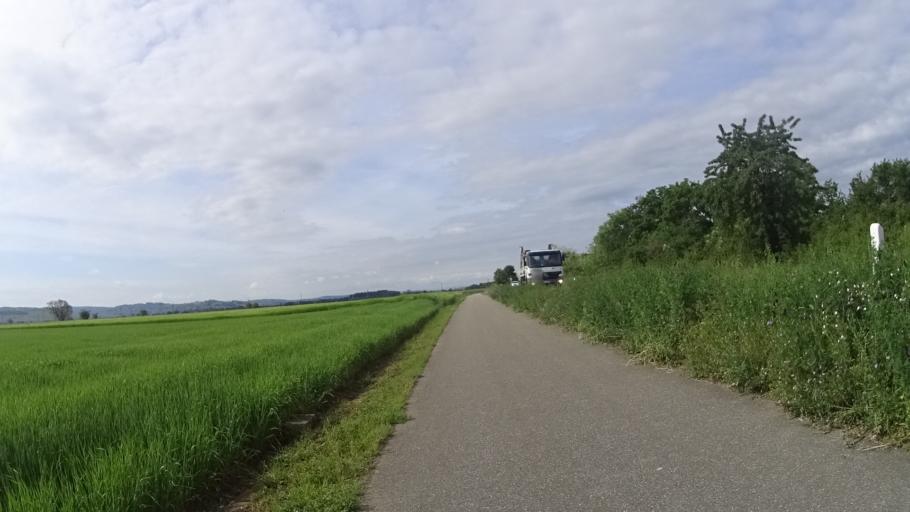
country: DE
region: Baden-Wuerttemberg
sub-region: Freiburg Region
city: Neuenburg am Rhein
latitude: 47.8025
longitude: 7.5617
